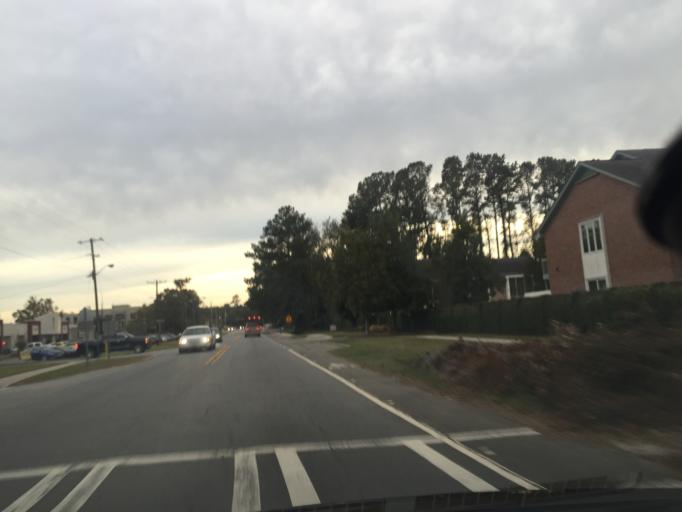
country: US
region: Georgia
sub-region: Chatham County
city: Isle of Hope
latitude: 32.0166
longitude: -81.1100
